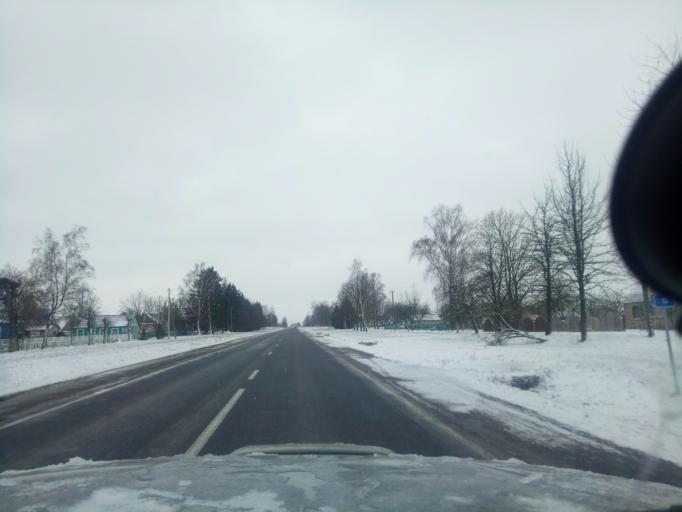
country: BY
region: Minsk
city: Klyetsk
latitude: 53.1223
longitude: 26.6667
